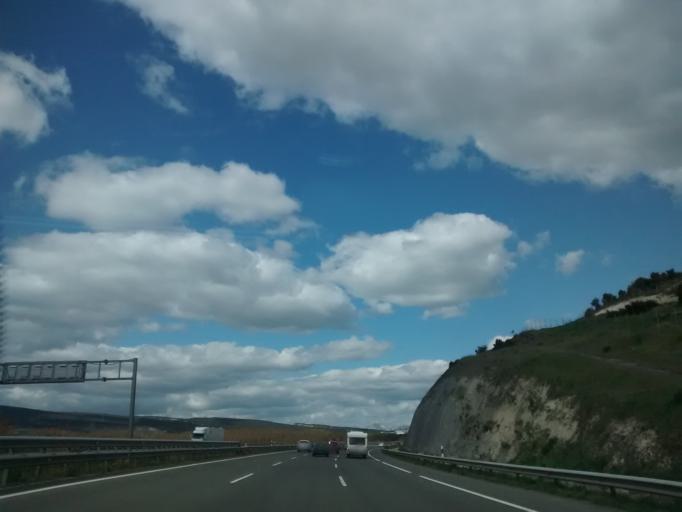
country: ES
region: Basque Country
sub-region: Provincia de Alava
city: Arminon
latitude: 42.7967
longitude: -2.8198
